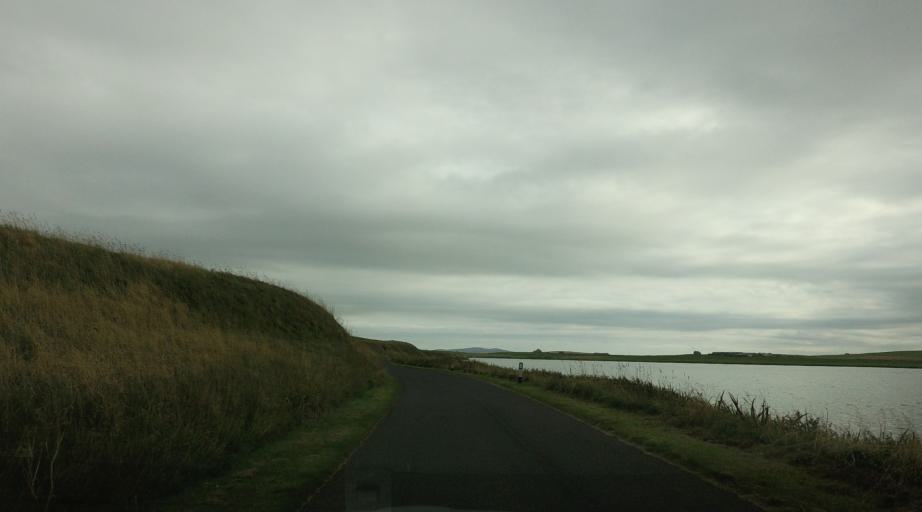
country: GB
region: Scotland
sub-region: Orkney Islands
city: Stromness
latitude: 59.0469
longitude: -3.3226
